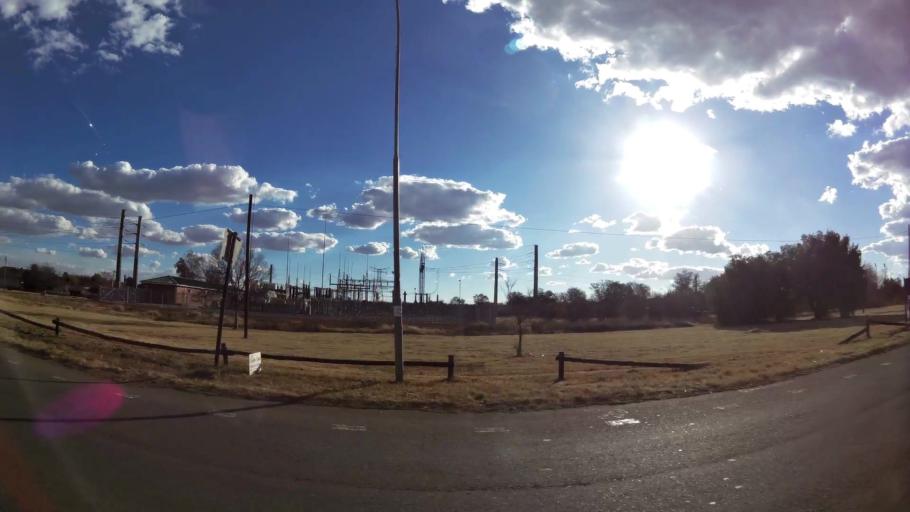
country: ZA
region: North-West
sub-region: Dr Kenneth Kaunda District Municipality
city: Potchefstroom
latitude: -26.7019
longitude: 27.1046
